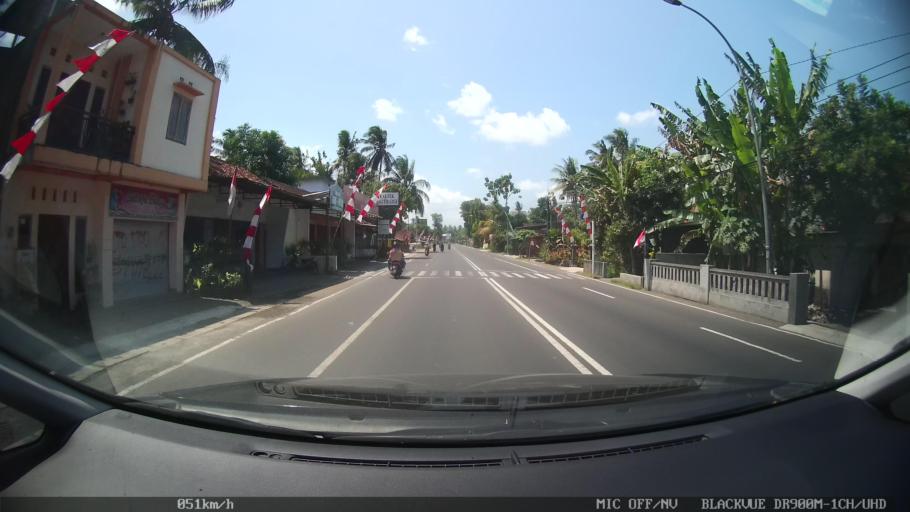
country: ID
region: Daerah Istimewa Yogyakarta
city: Srandakan
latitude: -7.9319
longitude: 110.2668
